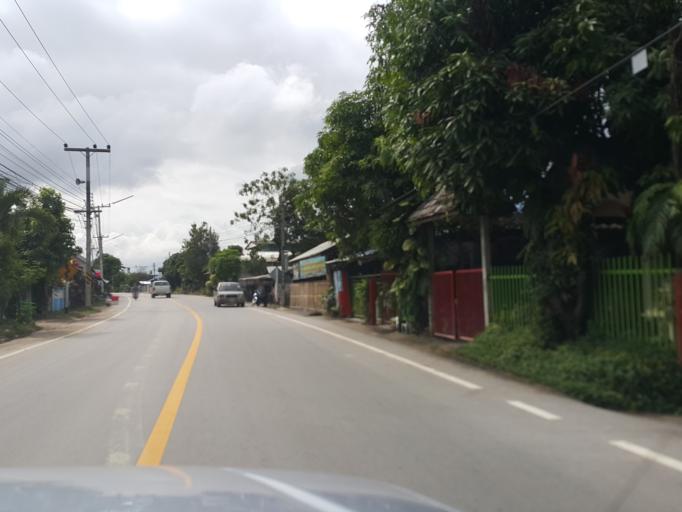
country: TH
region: Lamphun
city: Ban Thi
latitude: 18.6289
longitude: 99.1023
